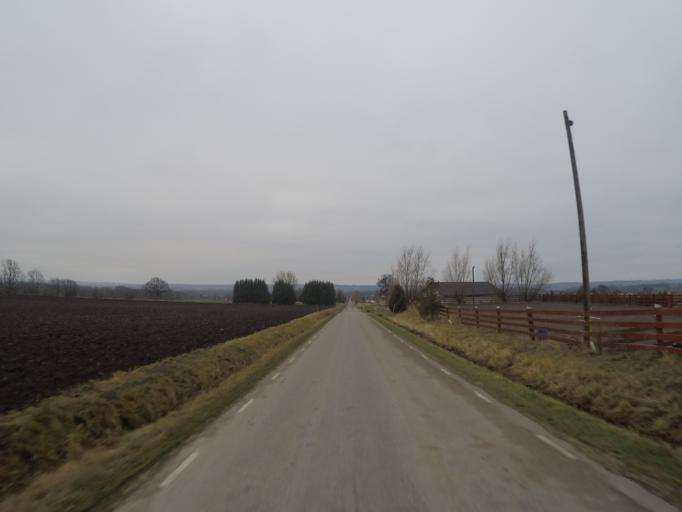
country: SE
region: Skane
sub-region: Hoors Kommun
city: Loberod
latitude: 55.7575
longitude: 13.4258
